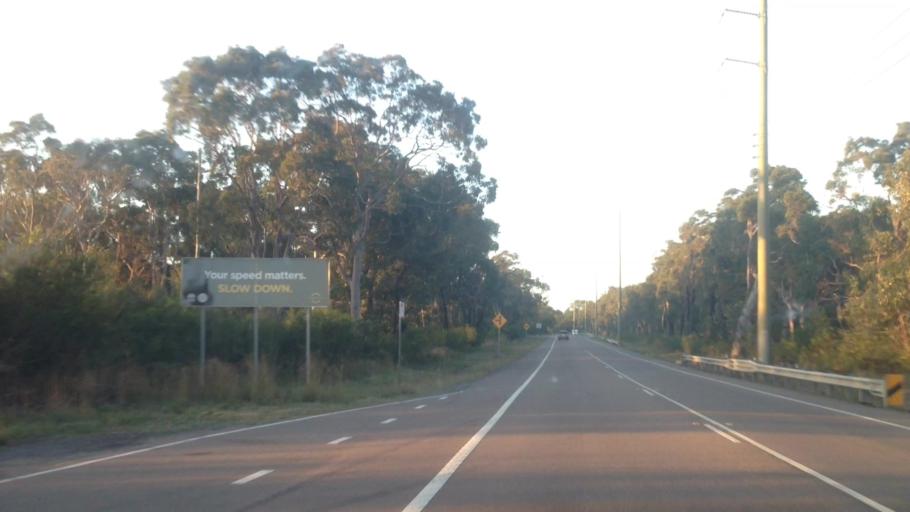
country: AU
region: New South Wales
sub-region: Wyong Shire
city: Kingfisher Shores
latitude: -33.1824
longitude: 151.5383
